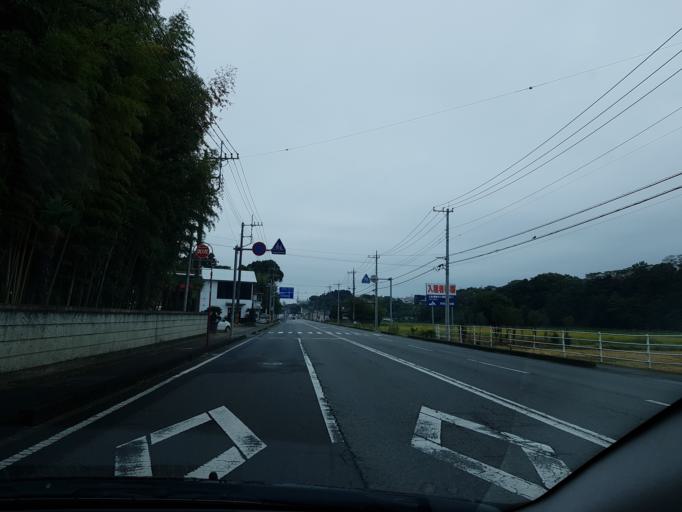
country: JP
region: Tochigi
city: Utsunomiya-shi
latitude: 36.5888
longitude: 139.8937
